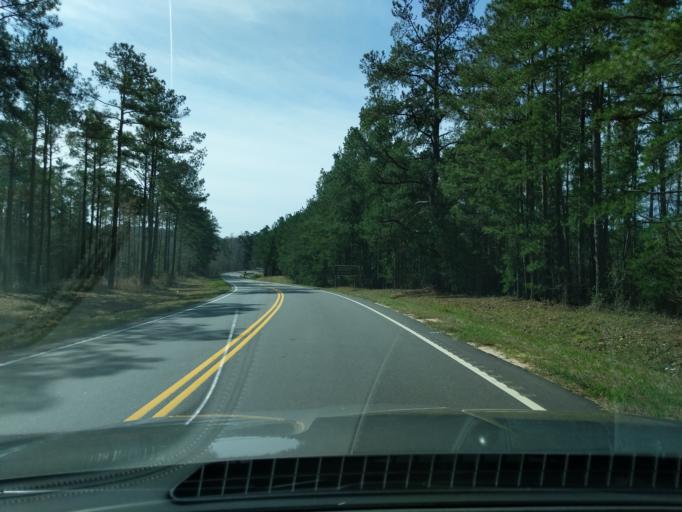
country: US
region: Georgia
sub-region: Columbia County
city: Evans
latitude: 33.6675
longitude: -82.1876
